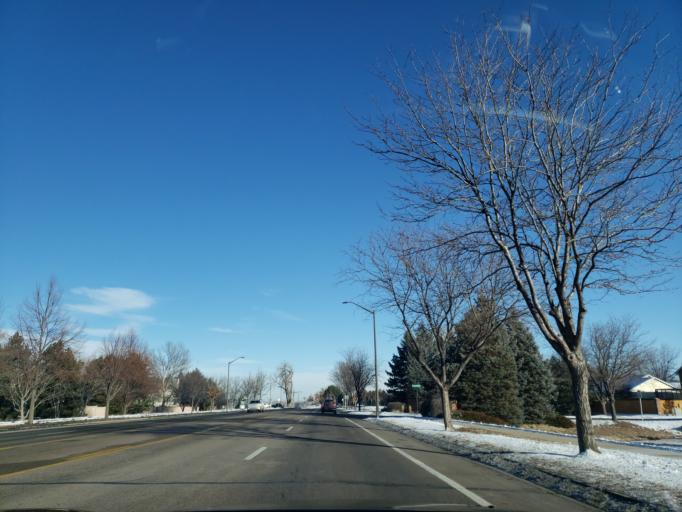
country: US
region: Colorado
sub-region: Larimer County
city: Fort Collins
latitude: 40.5378
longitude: -105.0228
